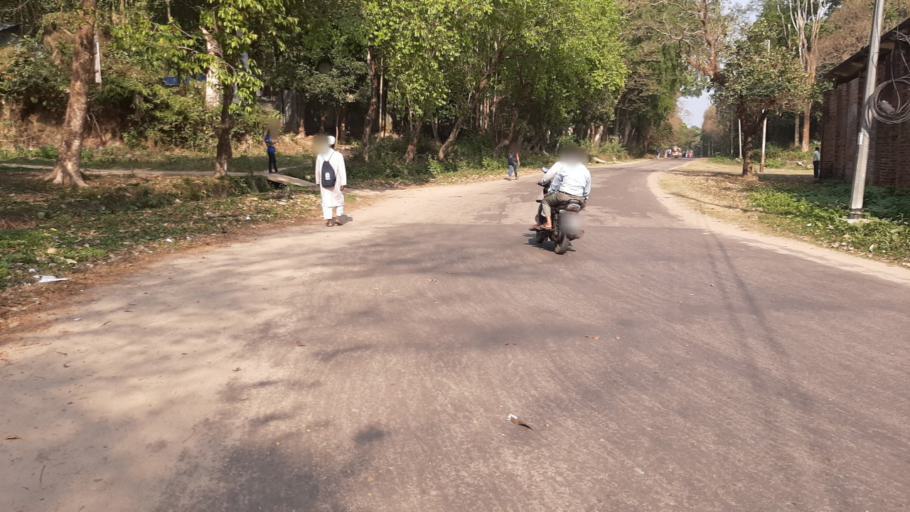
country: BD
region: Chittagong
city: Chittagong
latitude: 22.4743
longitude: 91.7887
